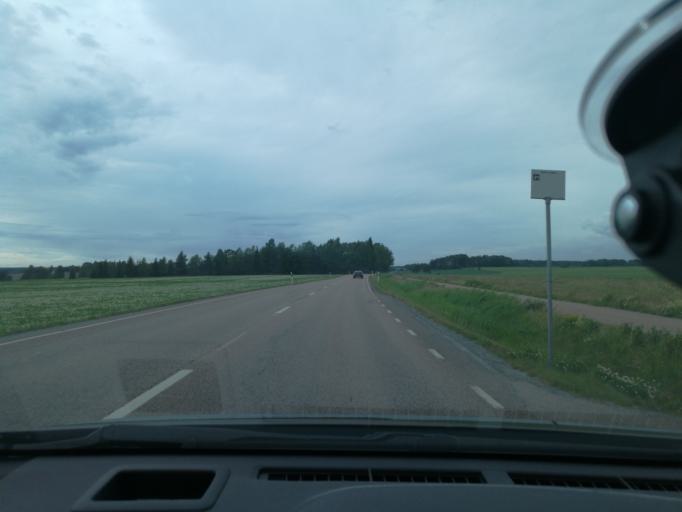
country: SE
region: Vaestmanland
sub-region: Vasteras
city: Skultuna
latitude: 59.6898
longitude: 16.4438
